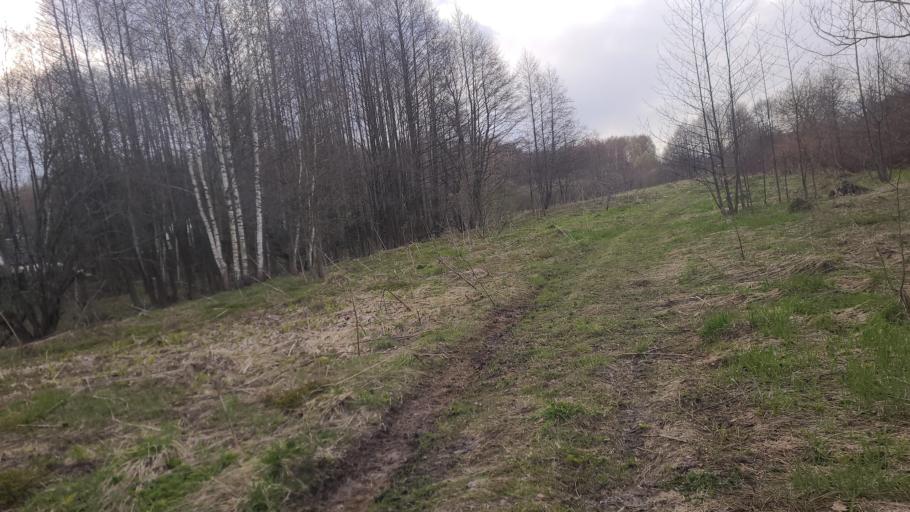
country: RU
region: Moskovskaya
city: Belyye Stolby
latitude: 55.3171
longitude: 37.8793
